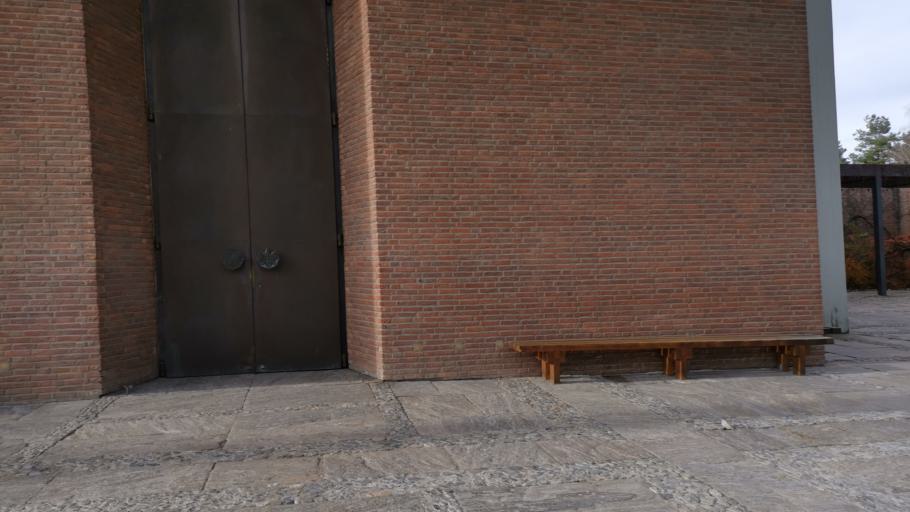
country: DE
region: Bavaria
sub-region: Upper Bavaria
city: Neuried
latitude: 48.0997
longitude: 11.4867
